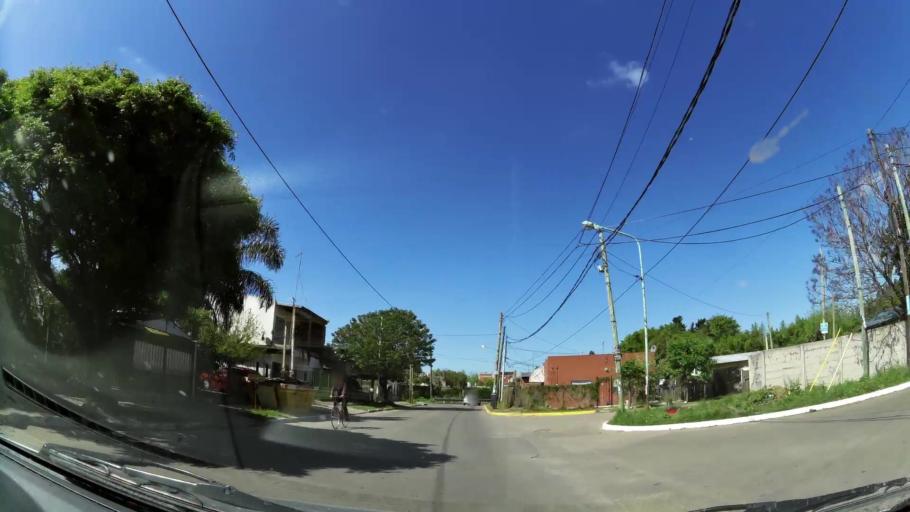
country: AR
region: Buenos Aires
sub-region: Partido de Quilmes
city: Quilmes
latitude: -34.8020
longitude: -58.2678
